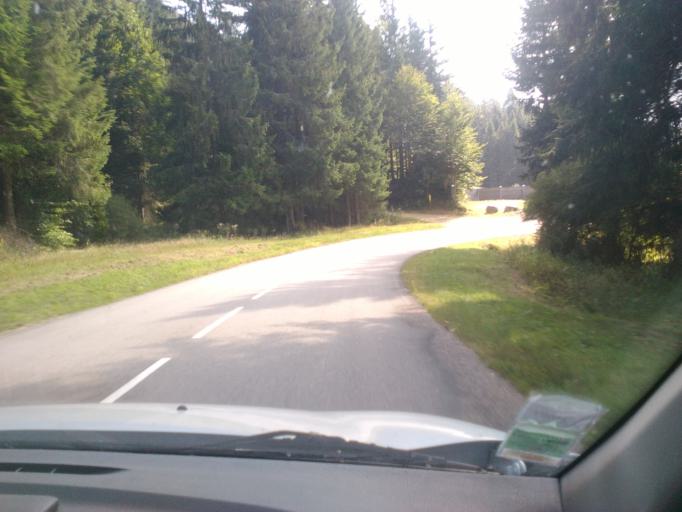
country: FR
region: Lorraine
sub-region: Departement des Vosges
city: Xonrupt-Longemer
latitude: 48.0445
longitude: 6.9340
